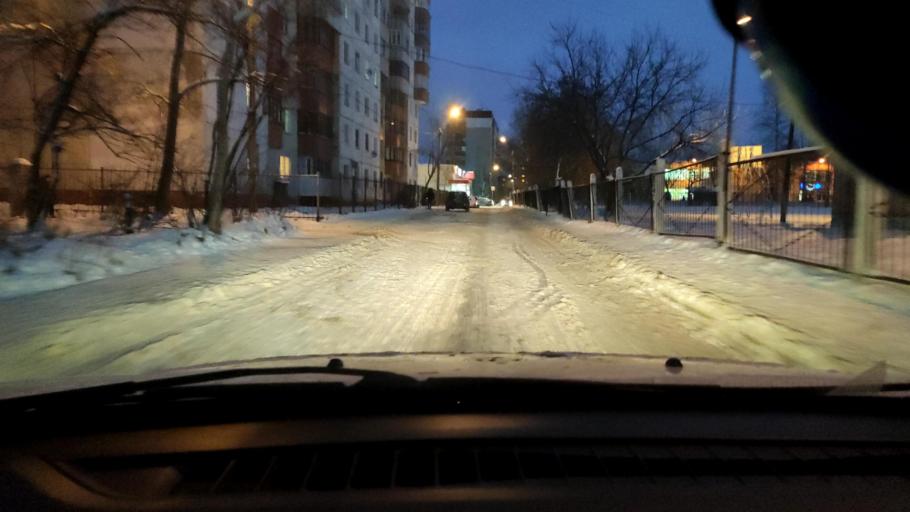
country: RU
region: Perm
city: Overyata
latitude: 58.0161
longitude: 55.9721
